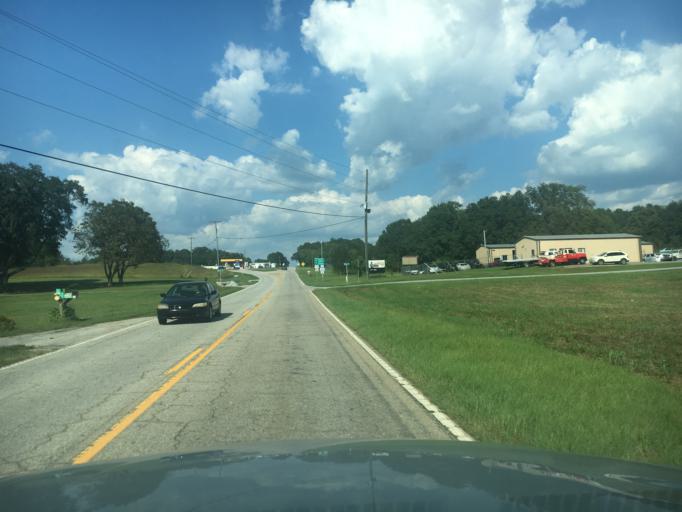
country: US
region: South Carolina
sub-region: Pickens County
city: Liberty
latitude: 34.7435
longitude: -82.6626
